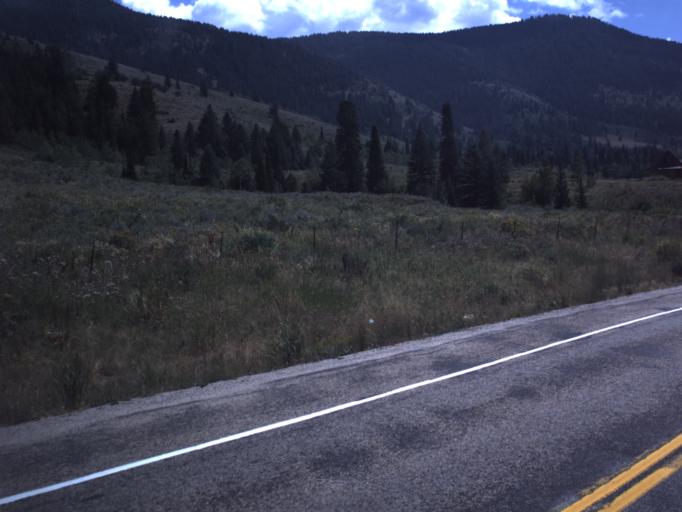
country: US
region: Utah
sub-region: Cache County
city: Richmond
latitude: 41.9276
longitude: -111.5611
